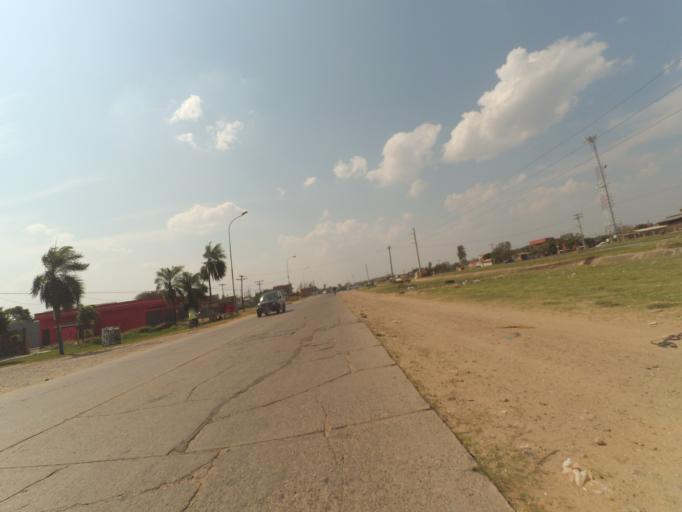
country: BO
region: Santa Cruz
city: Santa Cruz de la Sierra
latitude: -17.8669
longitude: -63.1900
